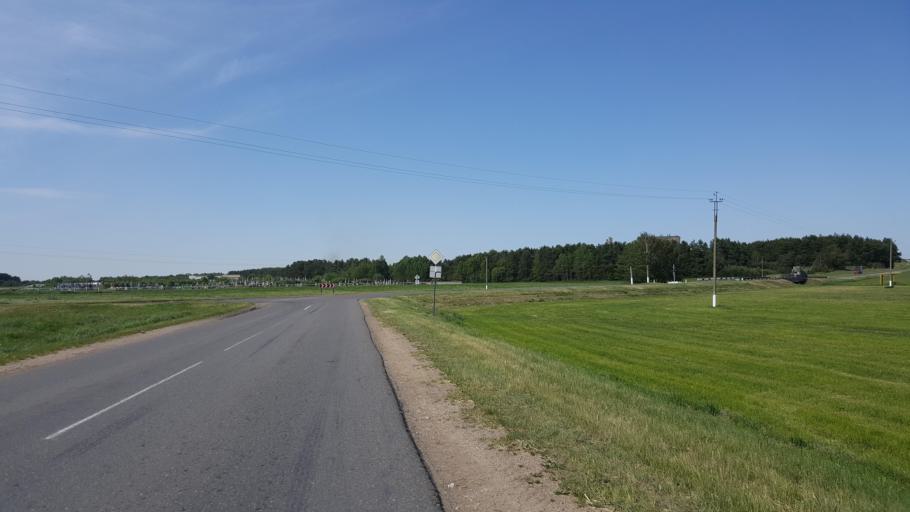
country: BY
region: Brest
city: Charnawchytsy
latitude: 52.2736
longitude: 23.5957
